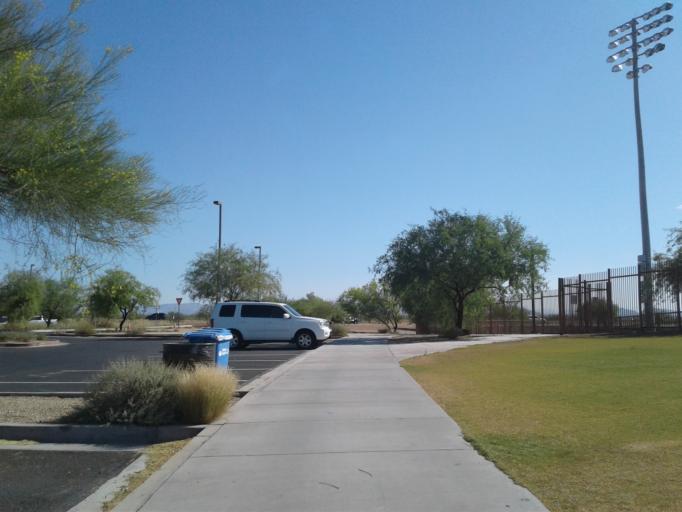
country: US
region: Arizona
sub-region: Maricopa County
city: Cave Creek
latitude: 33.6843
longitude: -112.0226
